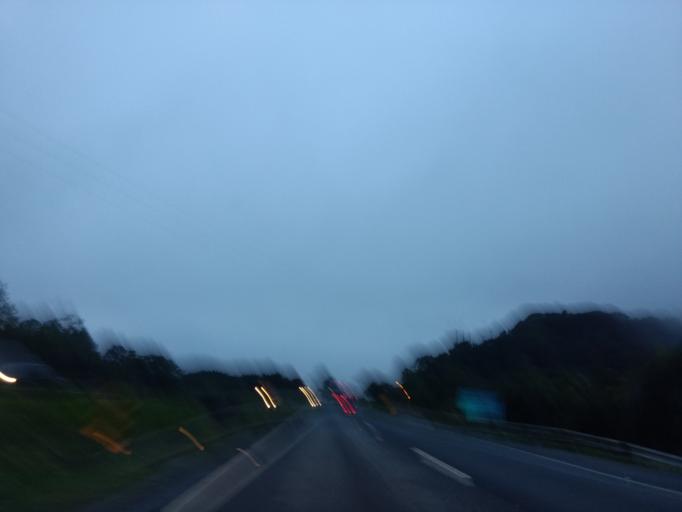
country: BR
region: Sao Paulo
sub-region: Juquia
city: Juquia
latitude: -24.3657
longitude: -47.6929
